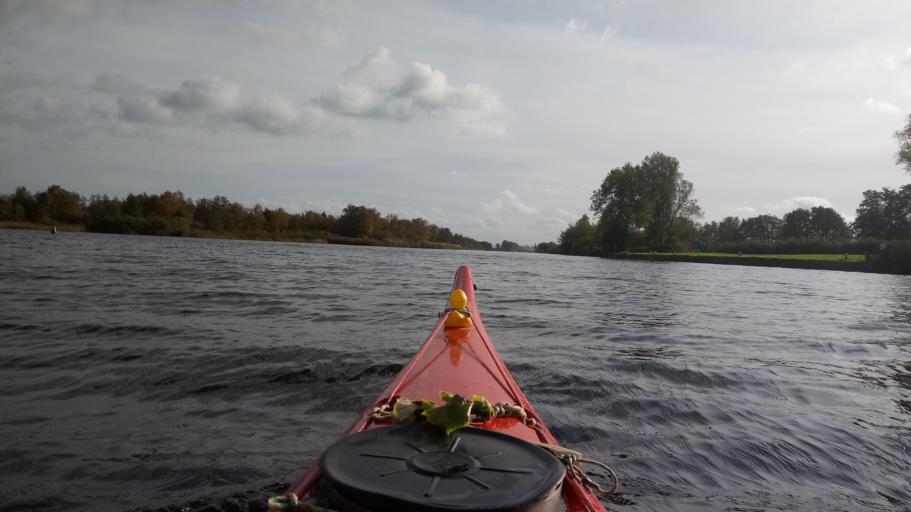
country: NL
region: Overijssel
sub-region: Gemeente Steenwijkerland
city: Wanneperveen
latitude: 52.6802
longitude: 6.0897
